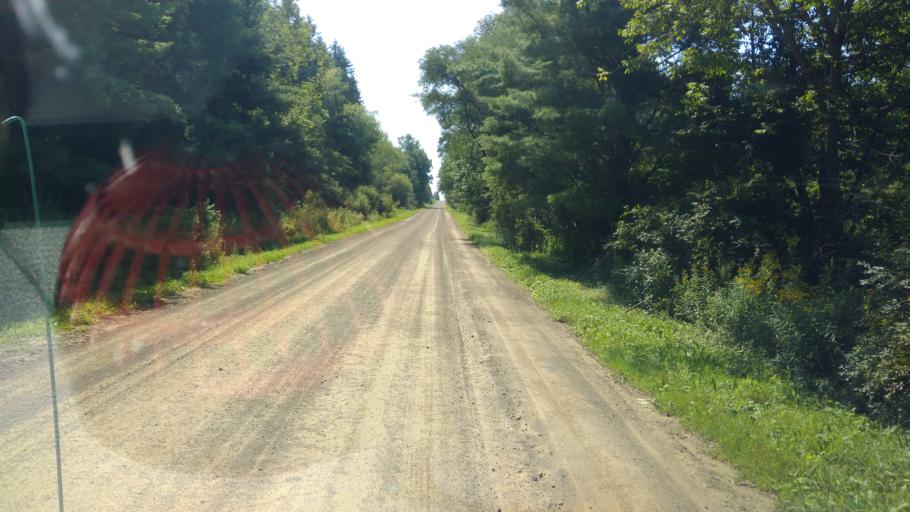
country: US
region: New York
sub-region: Allegany County
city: Houghton
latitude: 42.3634
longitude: -78.0404
